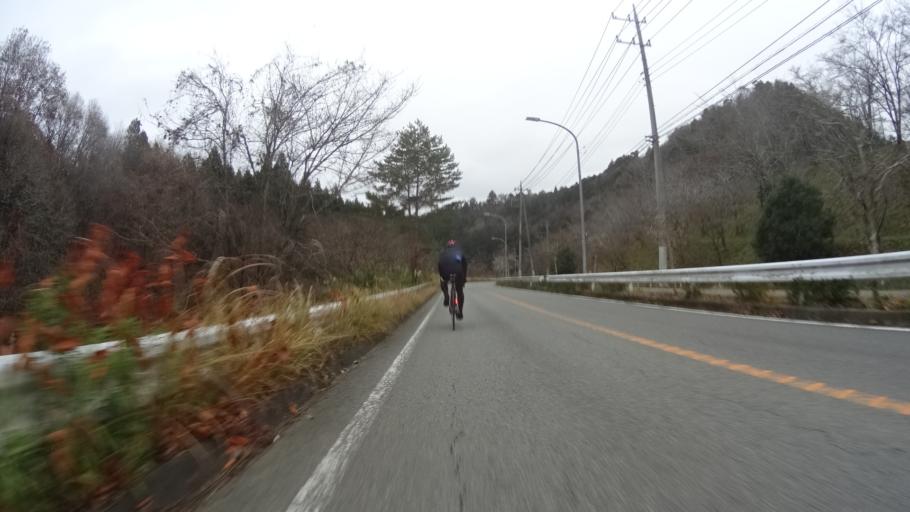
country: JP
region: Yamanashi
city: Uenohara
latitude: 35.6381
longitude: 139.1147
